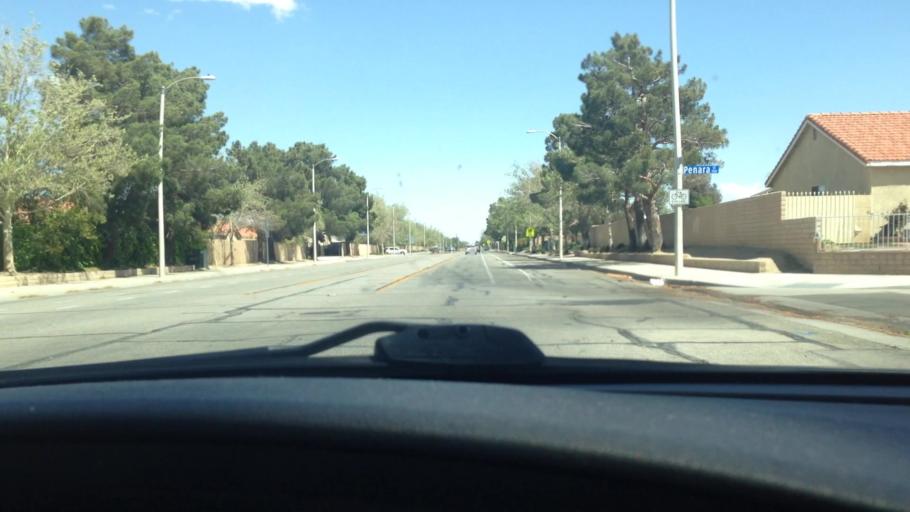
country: US
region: California
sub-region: Los Angeles County
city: Palmdale
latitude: 34.5656
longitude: -118.0579
